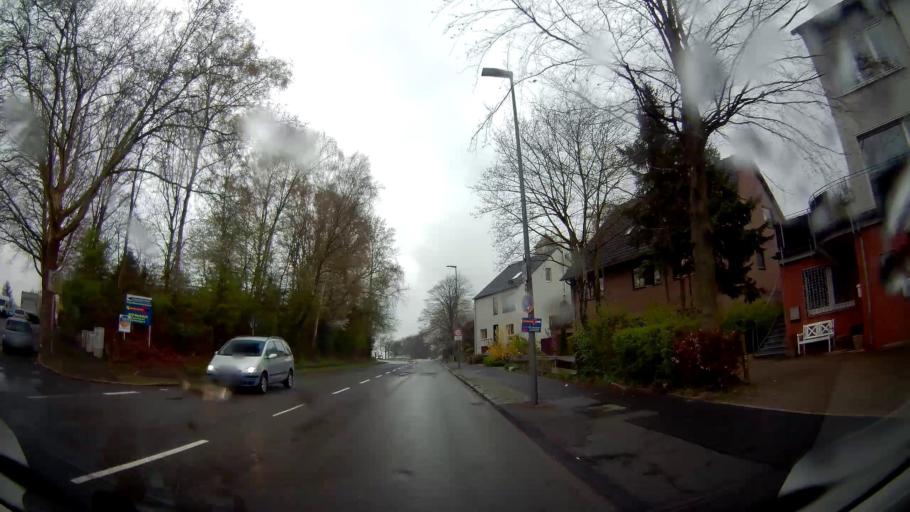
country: DE
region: North Rhine-Westphalia
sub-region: Regierungsbezirk Arnsberg
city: Bochum
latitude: 51.4993
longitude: 7.2751
